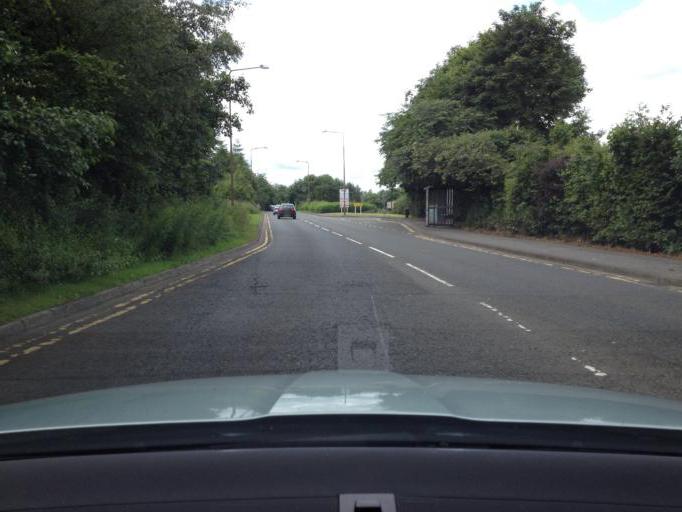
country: GB
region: Scotland
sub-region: West Lothian
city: Livingston
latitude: 55.8816
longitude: -3.5349
